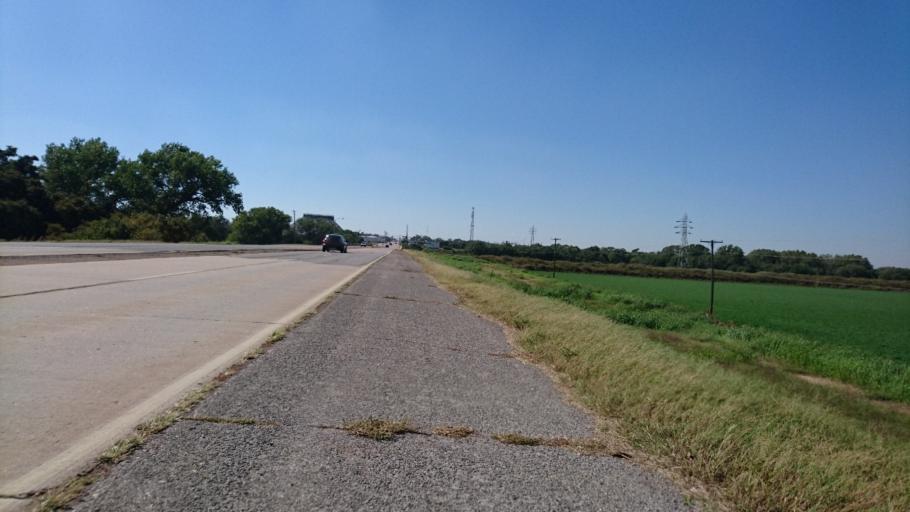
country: US
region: Oklahoma
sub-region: Custer County
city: Clinton
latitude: 35.5157
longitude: -98.9530
